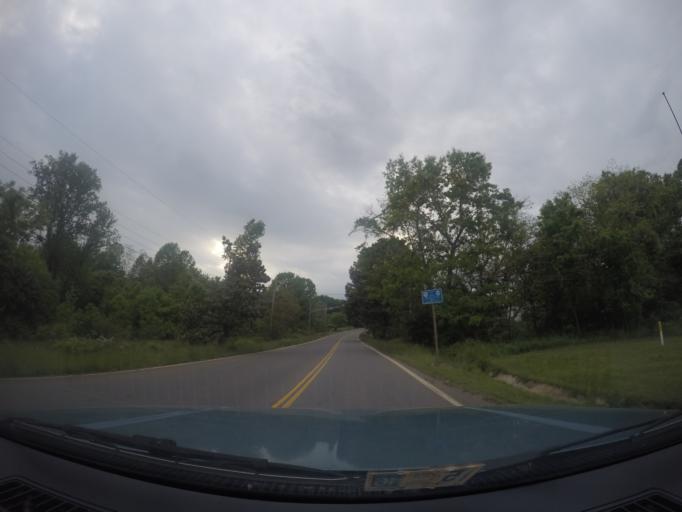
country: US
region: Virginia
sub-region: Amherst County
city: Madison Heights
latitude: 37.3893
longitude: -79.1015
